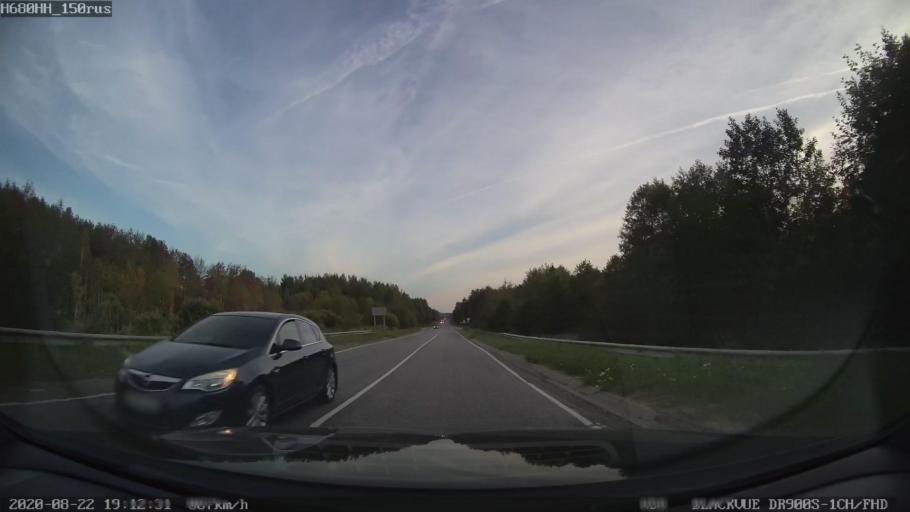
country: RU
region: Tverskaya
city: Sakharovo
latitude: 57.0034
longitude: 36.0284
